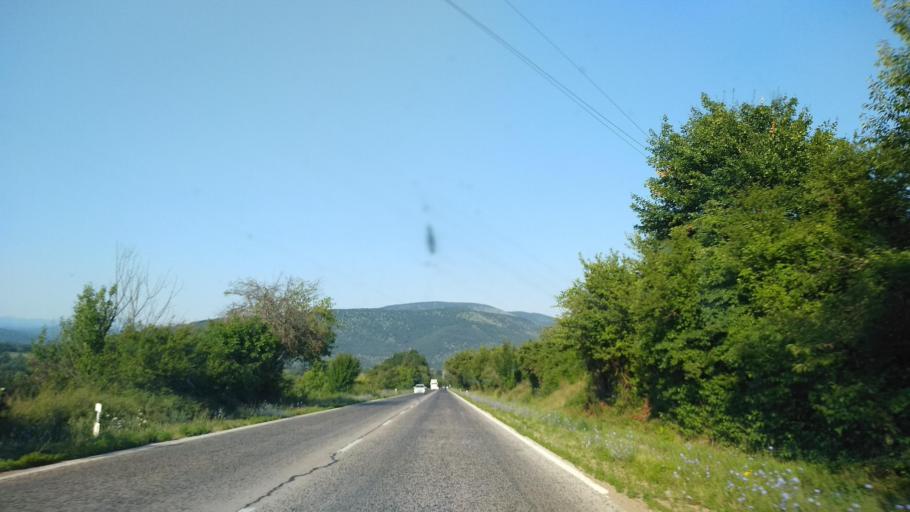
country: BG
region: Lovech
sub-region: Obshtina Lovech
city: Lovech
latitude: 43.0439
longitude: 24.7458
